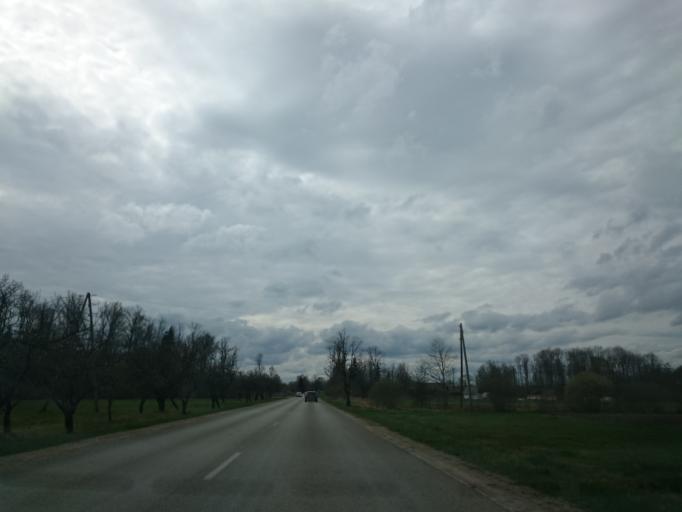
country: LV
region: Tukuma Rajons
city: Tukums
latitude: 56.9407
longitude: 23.1053
